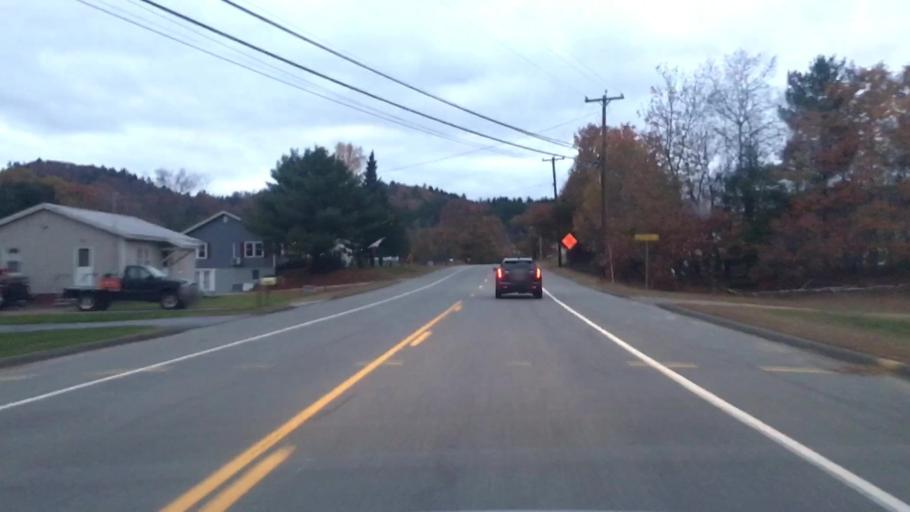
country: US
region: Maine
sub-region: Oxford County
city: Dixfield
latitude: 44.5248
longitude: -70.4583
